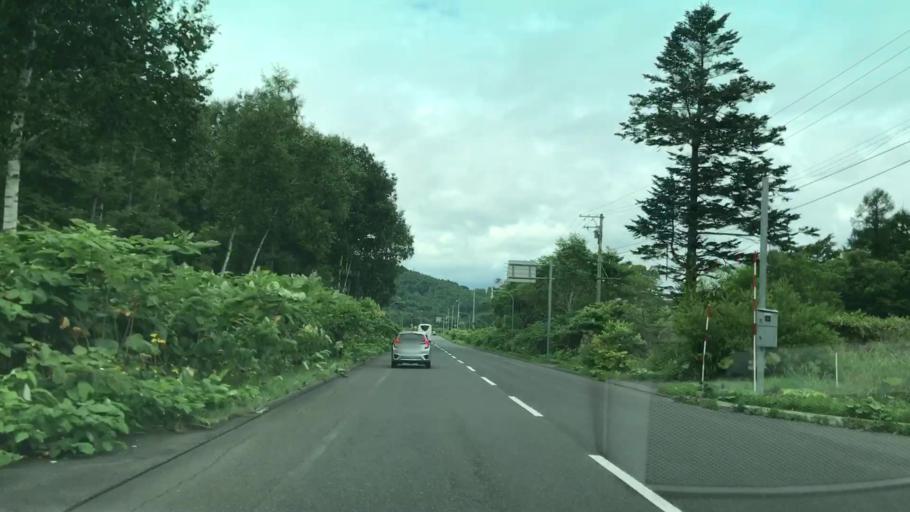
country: JP
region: Hokkaido
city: Niseko Town
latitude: 42.9471
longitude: 140.8465
